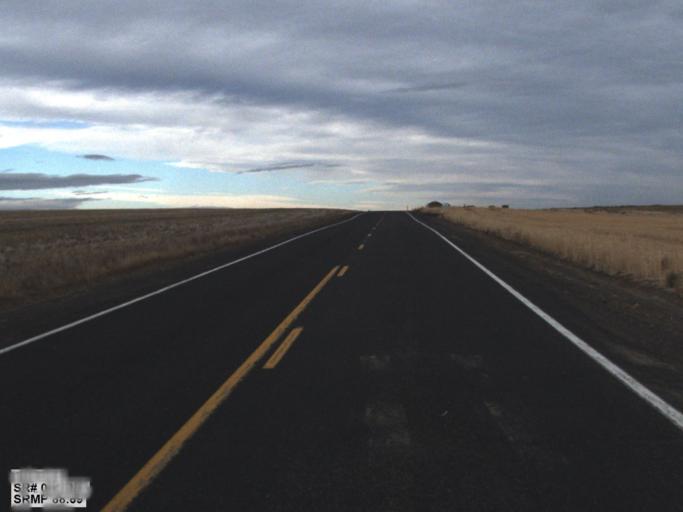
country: US
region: Washington
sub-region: Okanogan County
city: Coulee Dam
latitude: 47.7224
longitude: -118.7220
